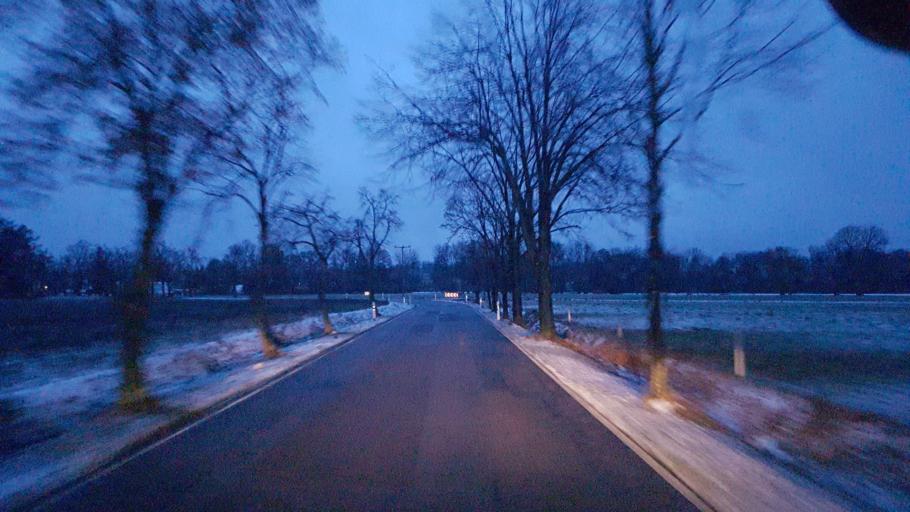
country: DE
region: Brandenburg
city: Guhrow
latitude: 51.7859
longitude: 14.2038
